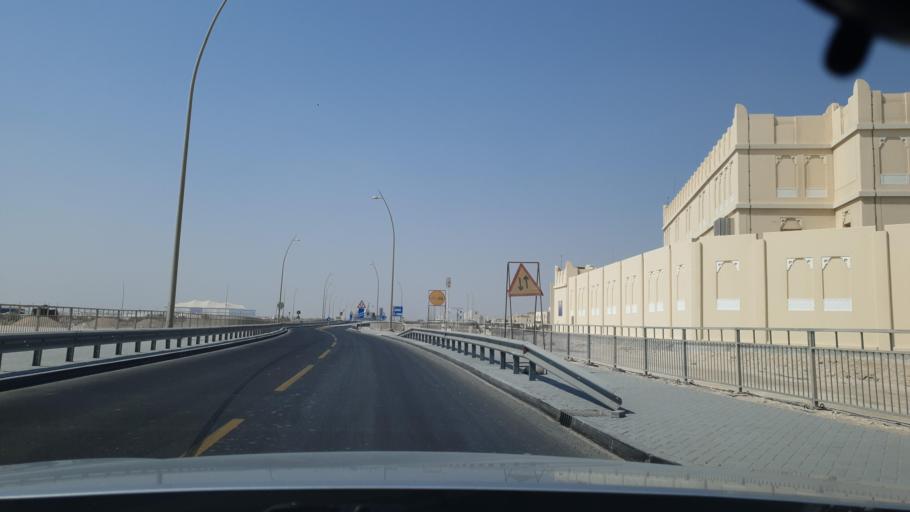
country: QA
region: Al Khawr
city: Al Khawr
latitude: 25.6672
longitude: 51.5190
